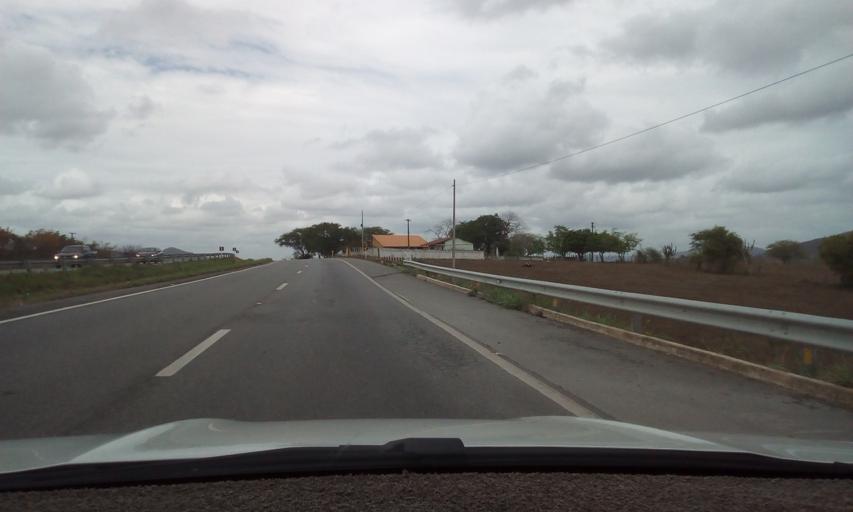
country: BR
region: Paraiba
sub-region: Gurinhem
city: Gurinhem
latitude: -7.1932
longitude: -35.4804
